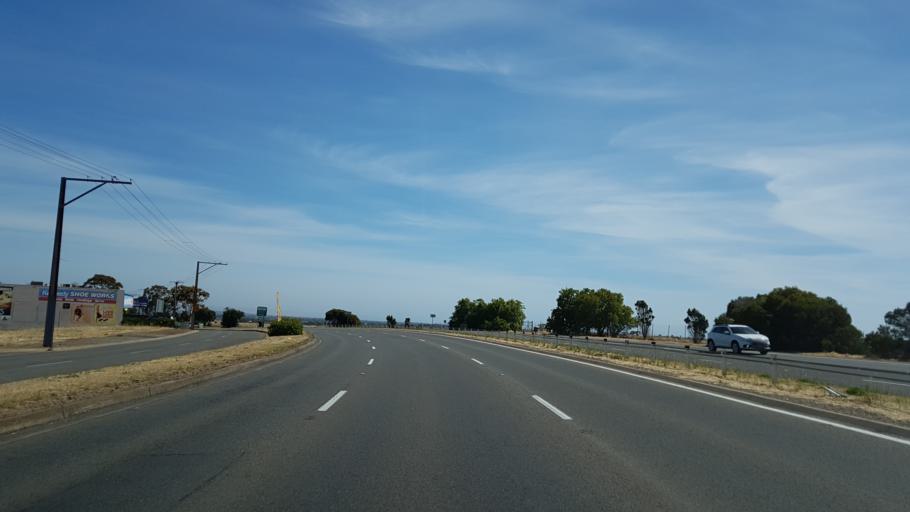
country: AU
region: South Australia
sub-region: Marion
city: Trott Park
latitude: -35.0638
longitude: 138.5555
